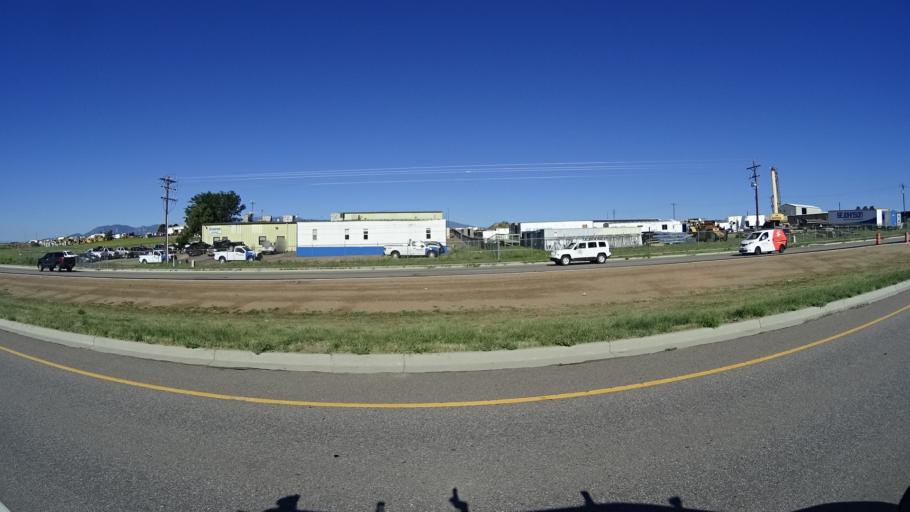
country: US
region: Colorado
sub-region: El Paso County
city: Cimarron Hills
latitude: 38.8762
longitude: -104.6825
